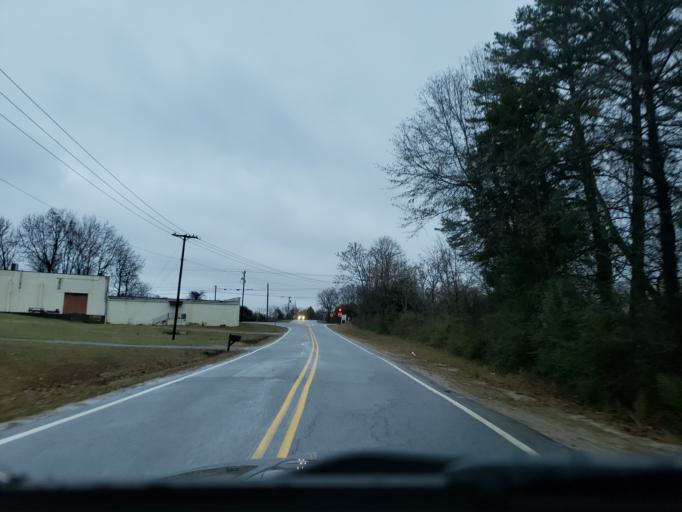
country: US
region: North Carolina
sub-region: Cleveland County
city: White Plains
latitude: 35.2008
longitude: -81.3891
